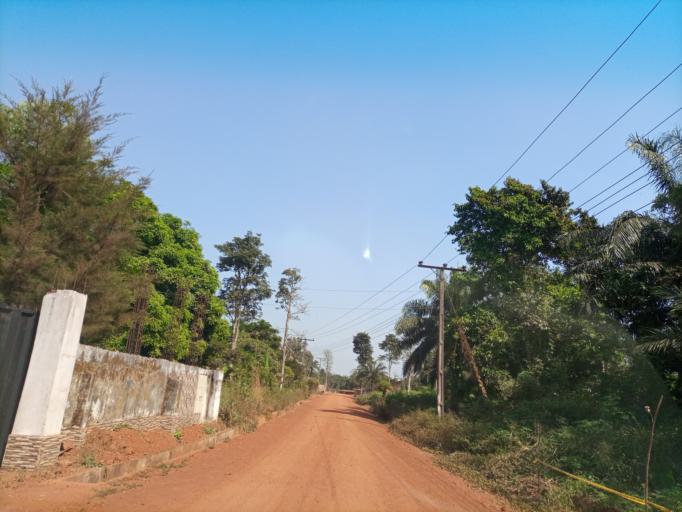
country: NG
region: Enugu
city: Nsukka
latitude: 6.7994
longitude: 7.3503
